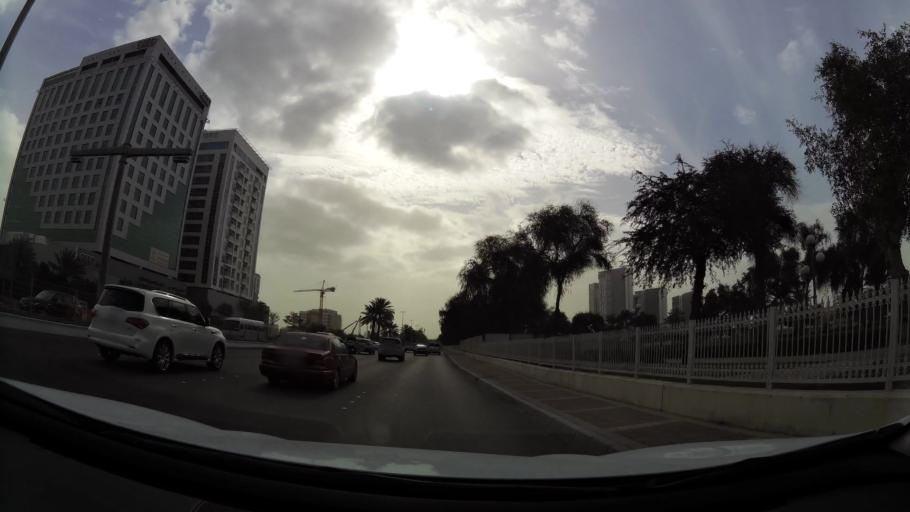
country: AE
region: Abu Dhabi
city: Abu Dhabi
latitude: 24.4205
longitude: 54.4592
